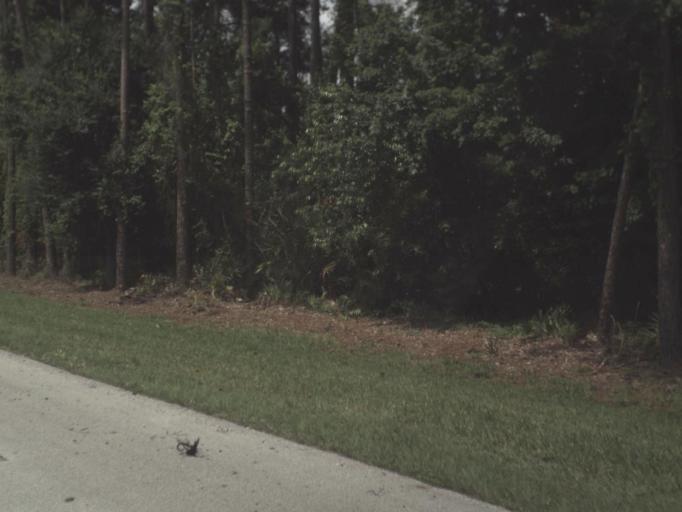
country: US
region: Florida
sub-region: Saint Johns County
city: Saint Augustine South
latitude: 29.8348
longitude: -81.3836
